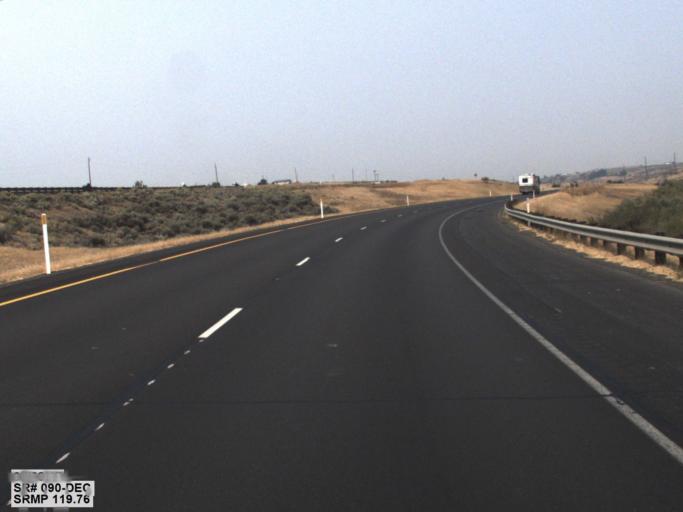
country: US
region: Washington
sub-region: Kittitas County
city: Kittitas
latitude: 46.9614
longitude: -120.3275
